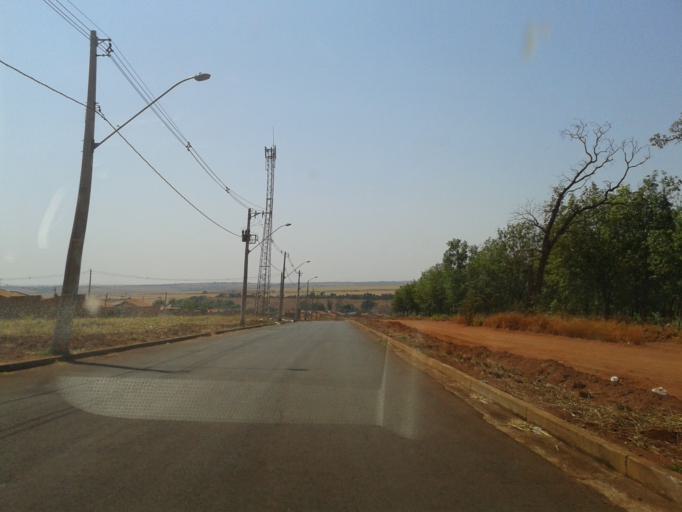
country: BR
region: Minas Gerais
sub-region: Ituiutaba
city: Ituiutaba
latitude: -19.0174
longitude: -49.4562
